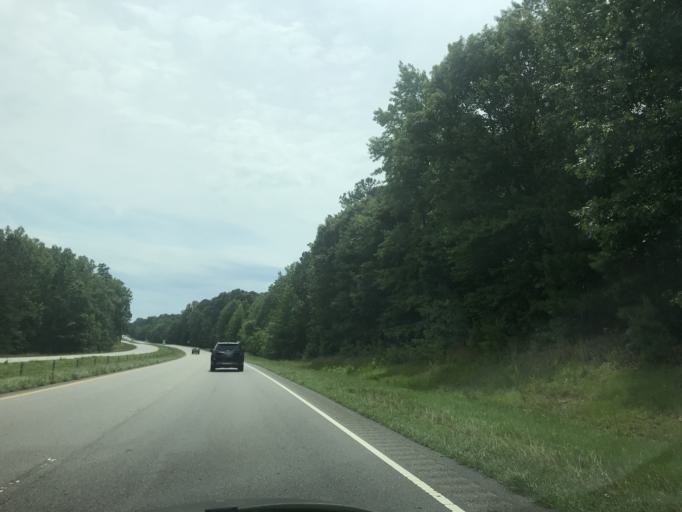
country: US
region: North Carolina
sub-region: Vance County
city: South Henderson
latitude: 36.2694
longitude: -78.4129
